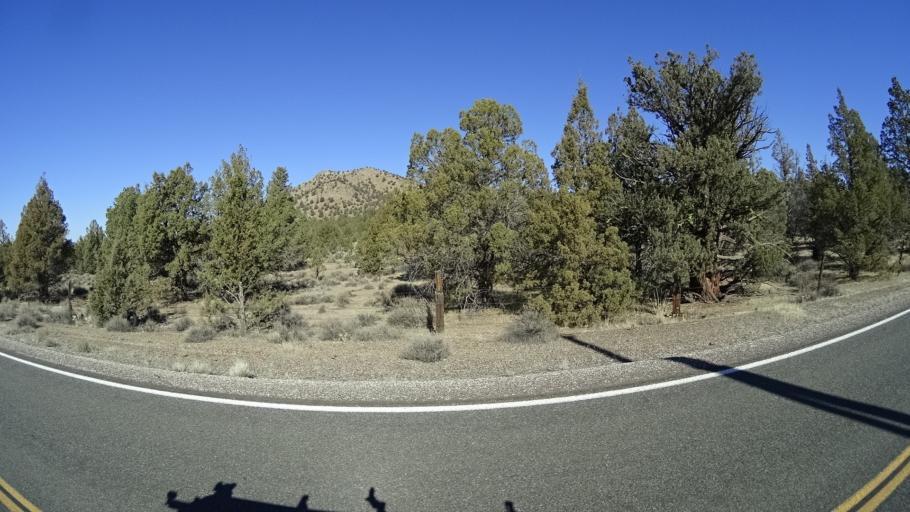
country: US
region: California
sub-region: Siskiyou County
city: Montague
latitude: 41.6600
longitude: -122.3831
